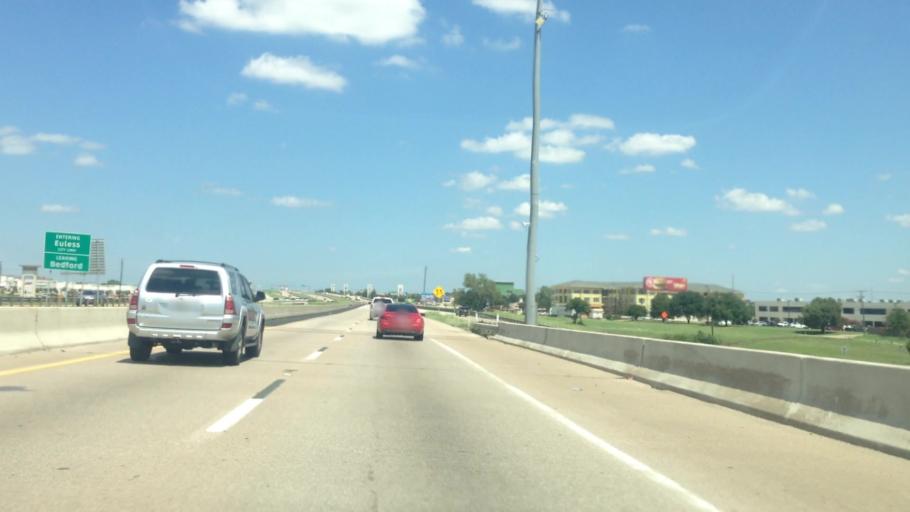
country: US
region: Texas
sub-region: Tarrant County
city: Euless
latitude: 32.8668
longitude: -97.1013
